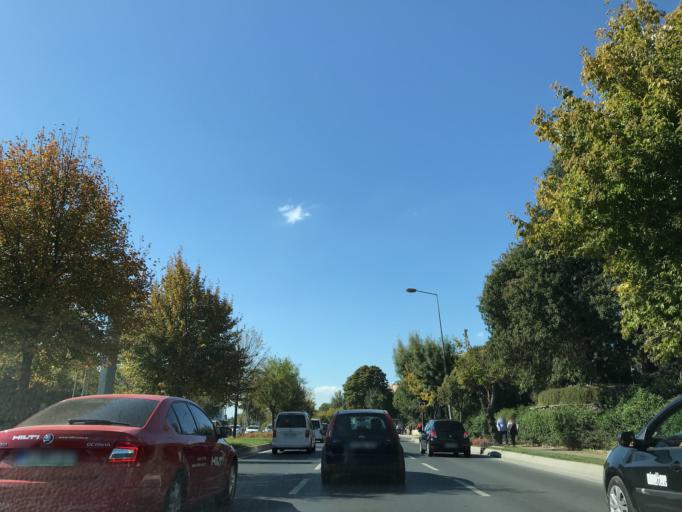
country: TR
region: Istanbul
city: Bahcelievler
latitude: 40.9745
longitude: 28.8732
